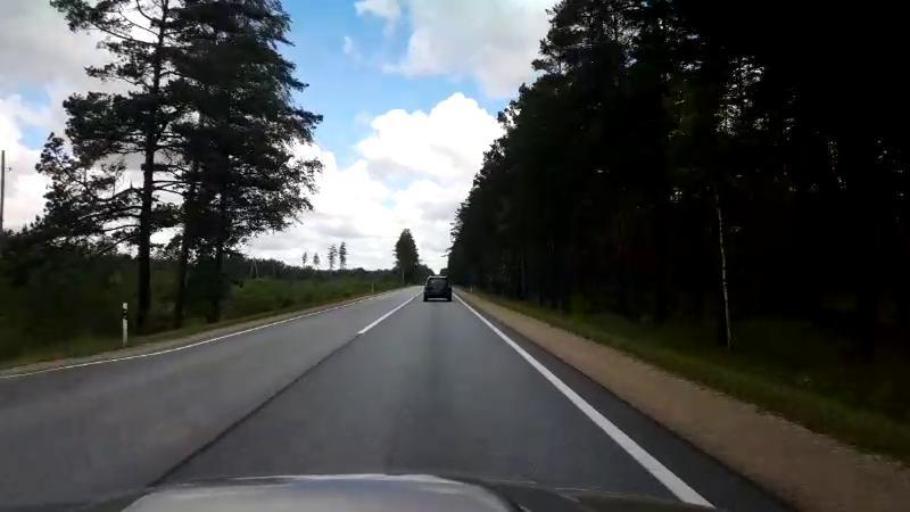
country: LV
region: Salaspils
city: Salaspils
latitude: 56.9349
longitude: 24.3865
